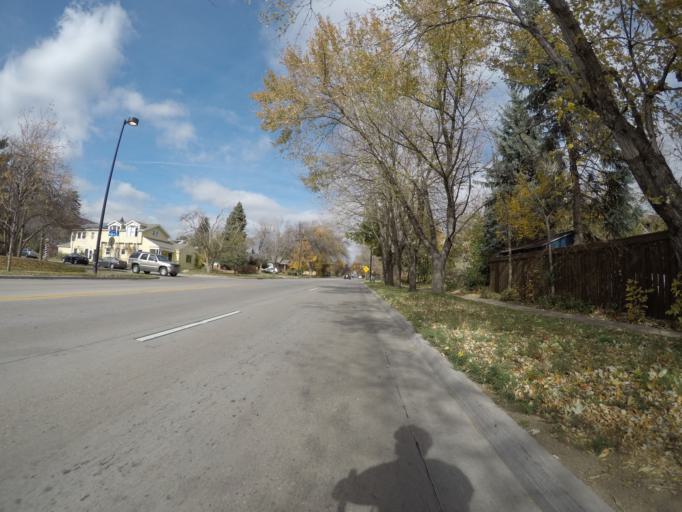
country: US
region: Colorado
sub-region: Boulder County
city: Boulder
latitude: 40.0308
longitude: -105.2820
